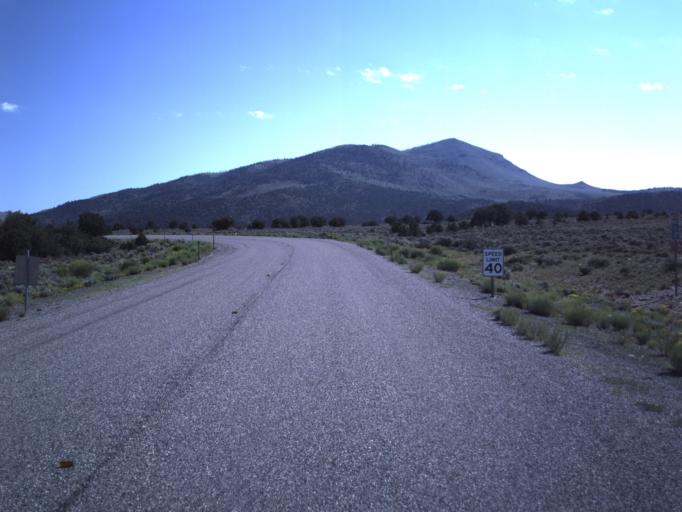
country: US
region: Utah
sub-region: Wayne County
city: Loa
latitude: 38.4930
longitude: -111.5371
